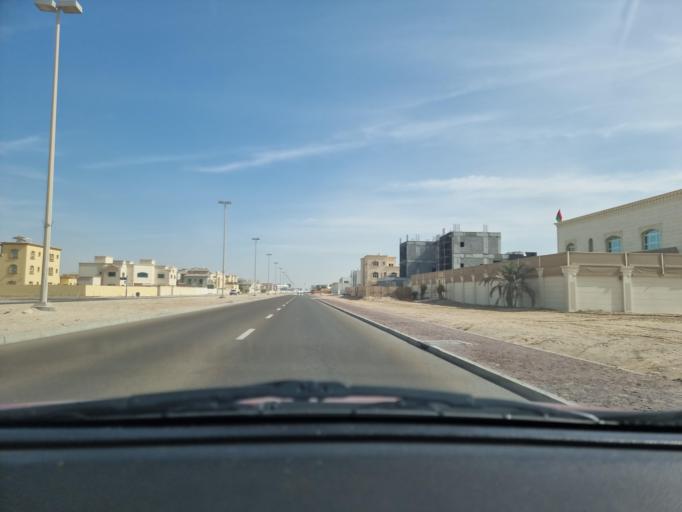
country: AE
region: Abu Dhabi
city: Abu Dhabi
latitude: 24.3153
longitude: 54.5433
